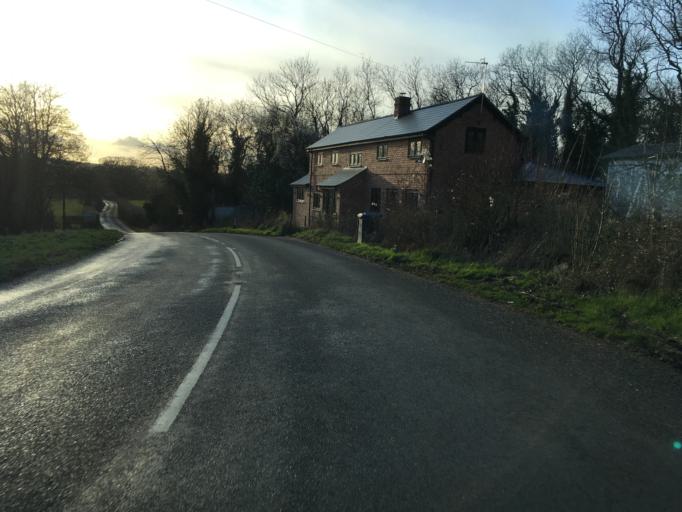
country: GB
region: England
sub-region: Warwickshire
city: Henley in Arden
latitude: 52.2541
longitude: -1.7939
